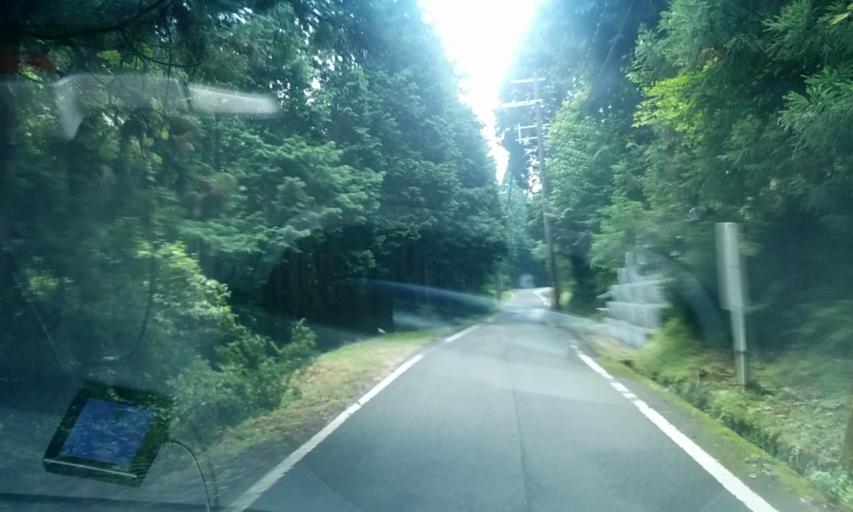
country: JP
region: Hyogo
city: Sasayama
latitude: 35.1841
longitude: 135.2162
